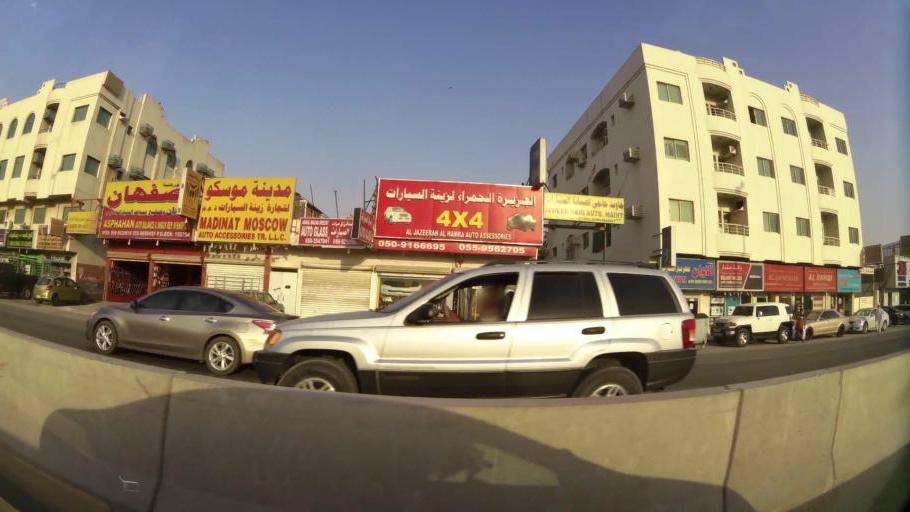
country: AE
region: Ash Shariqah
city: Sharjah
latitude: 25.3239
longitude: 55.4047
